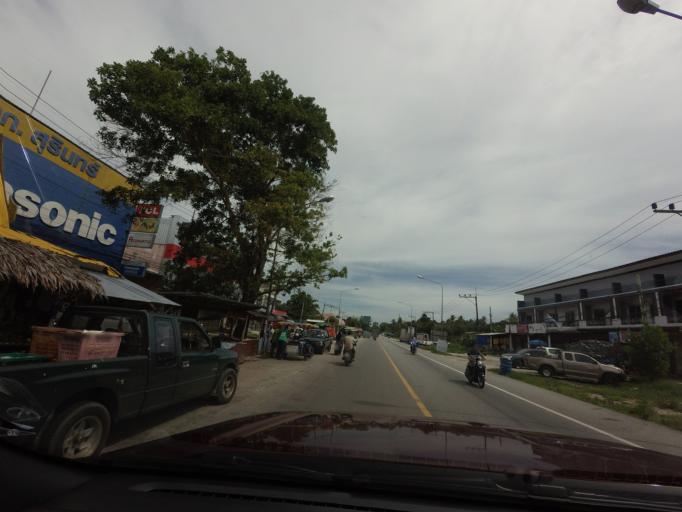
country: TH
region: Narathiwat
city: Tak Bai
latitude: 6.2562
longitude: 102.0493
